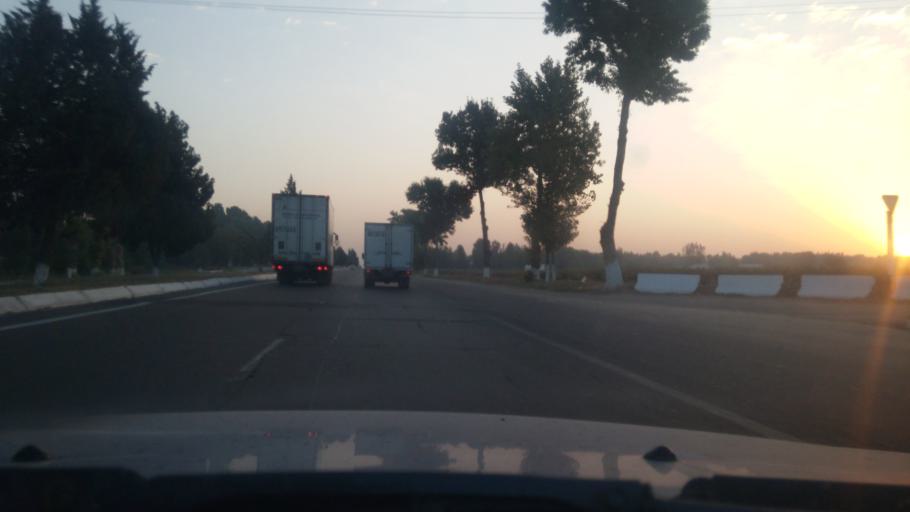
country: UZ
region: Toshkent
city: Zafar
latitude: 41.0364
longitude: 68.8754
